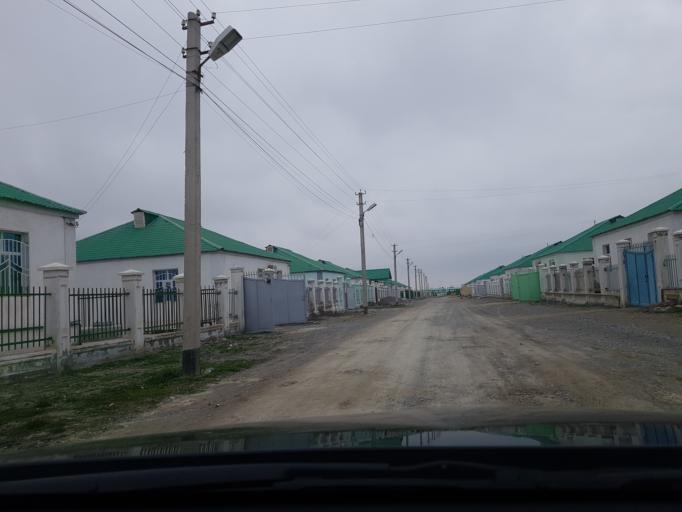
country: TM
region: Ahal
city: Arcabil
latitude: 38.1300
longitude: 57.9417
